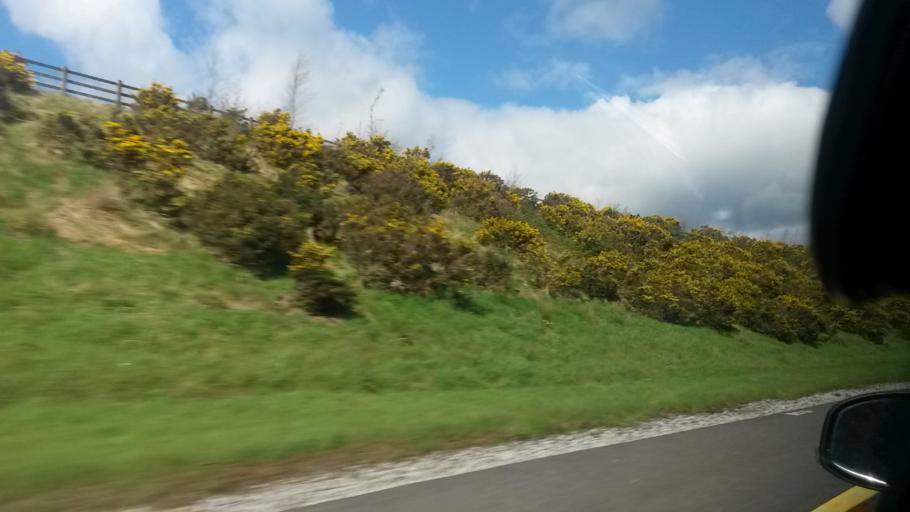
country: IE
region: Munster
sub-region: County Cork
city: Mitchelstown
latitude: 52.2204
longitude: -8.2864
